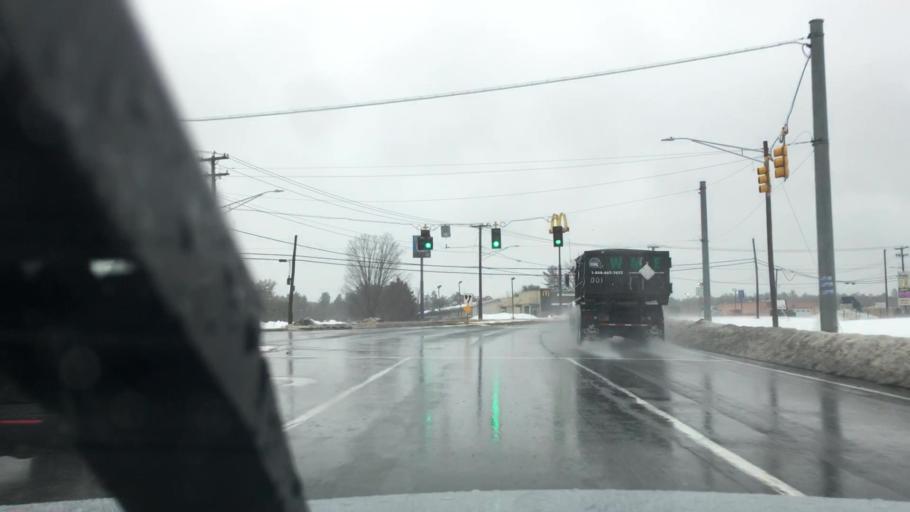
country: US
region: Massachusetts
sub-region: Hampden County
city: North Chicopee
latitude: 42.1652
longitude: -72.5465
